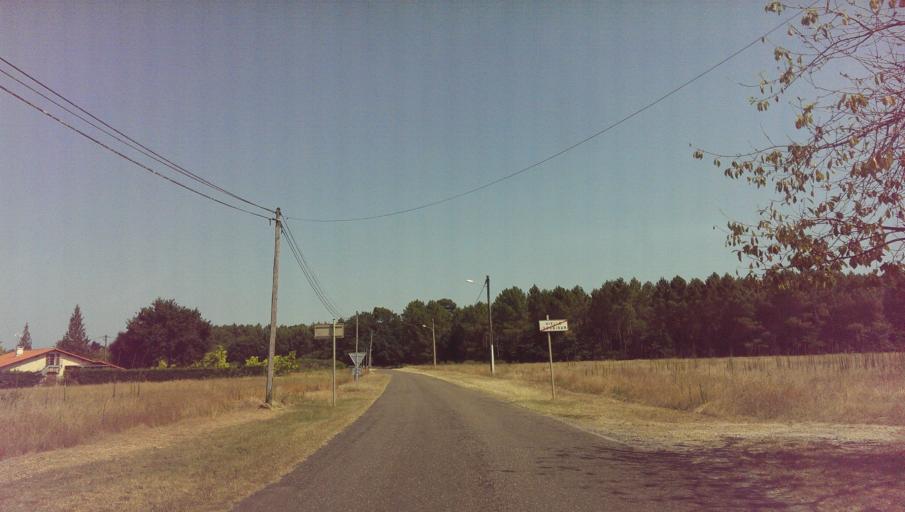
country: FR
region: Aquitaine
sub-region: Departement des Landes
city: Sarbazan
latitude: 44.0454
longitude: -0.1853
